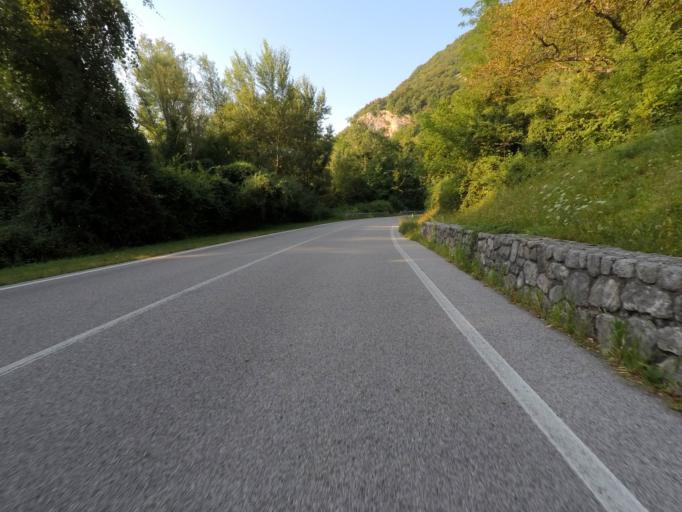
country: IT
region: Friuli Venezia Giulia
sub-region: Provincia di Udine
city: Osoppo
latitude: 46.2504
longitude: 13.0367
